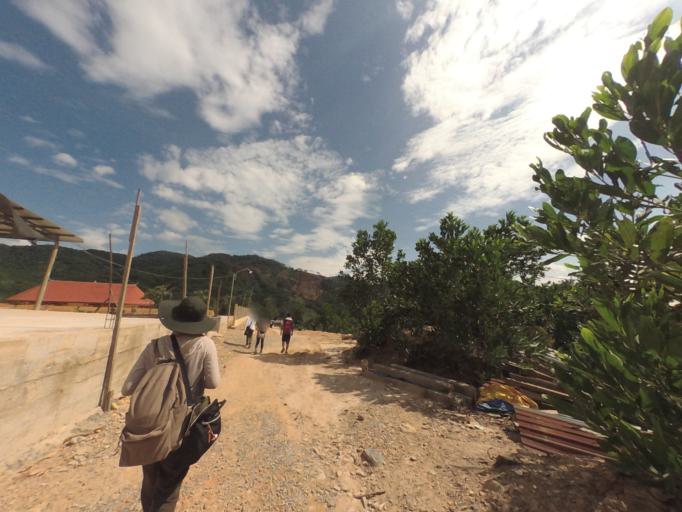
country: VN
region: Thua Thien-Hue
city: A Luoi
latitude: 16.3020
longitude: 107.3250
